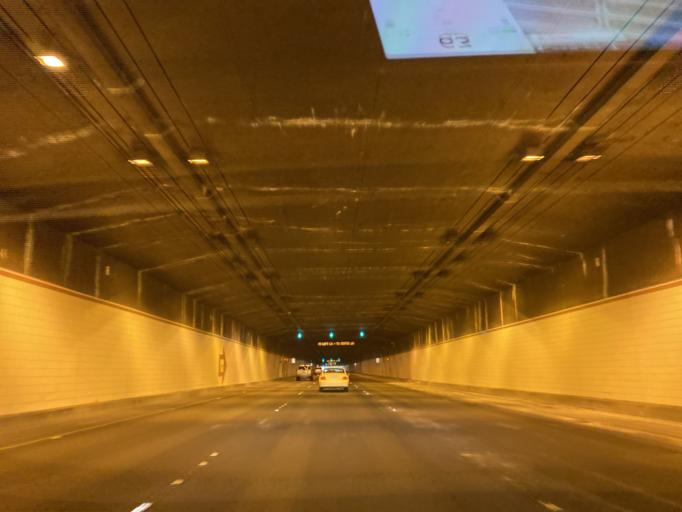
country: US
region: Nevada
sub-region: Clark County
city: Paradise
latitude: 36.0737
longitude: -115.1452
